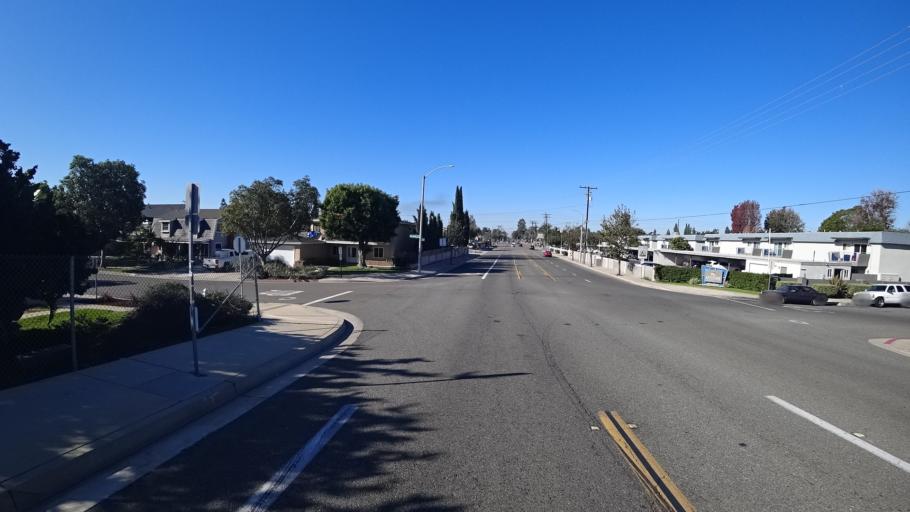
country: US
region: California
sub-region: Orange County
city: Tustin
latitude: 33.7671
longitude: -117.8331
